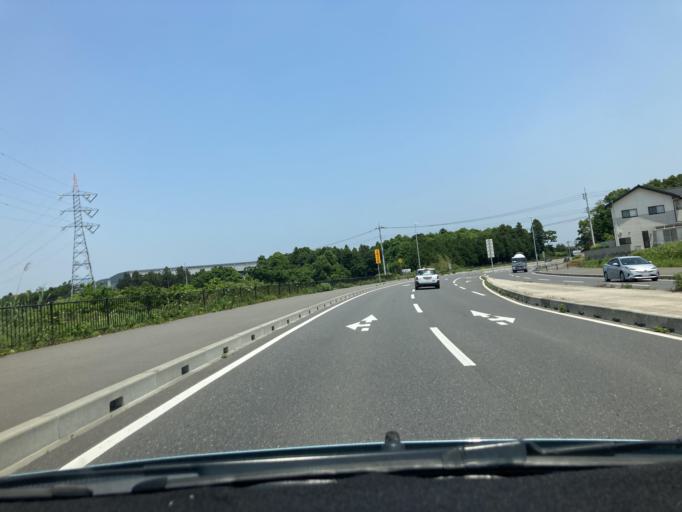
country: JP
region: Ibaraki
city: Mitsukaido
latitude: 36.0811
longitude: 140.0627
